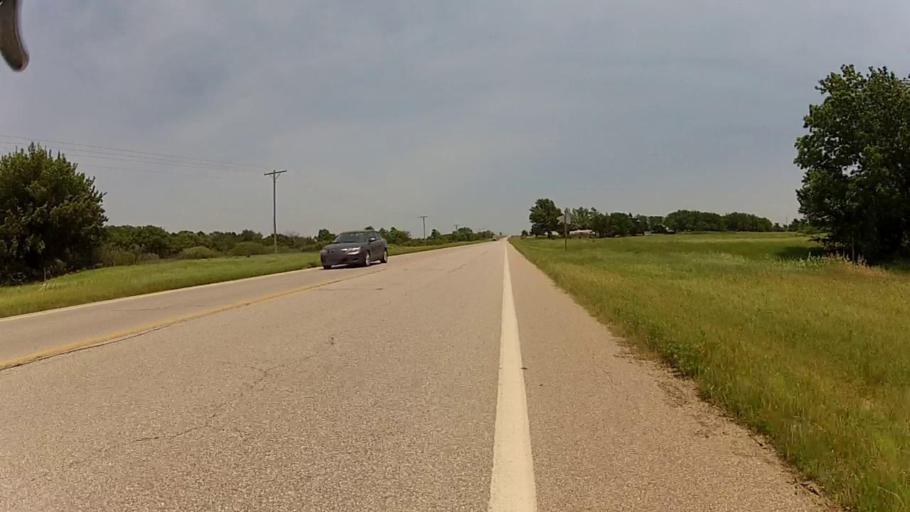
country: US
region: Kansas
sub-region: Cowley County
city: Arkansas City
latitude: 37.0563
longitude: -97.1174
